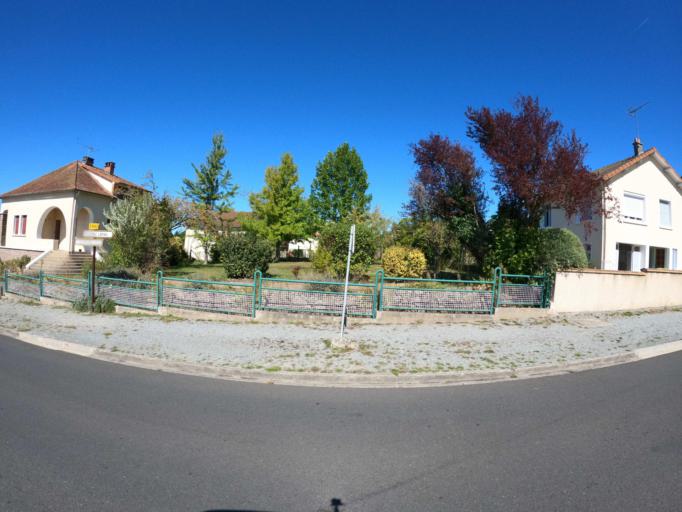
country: FR
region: Limousin
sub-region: Departement de la Haute-Vienne
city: Le Dorat
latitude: 46.2144
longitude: 1.0879
